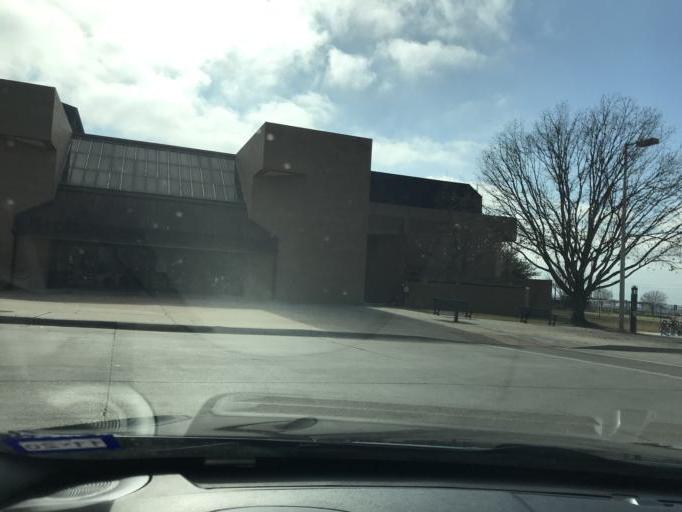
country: US
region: Texas
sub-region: Denton County
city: Denton
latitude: 33.2116
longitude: -97.1530
